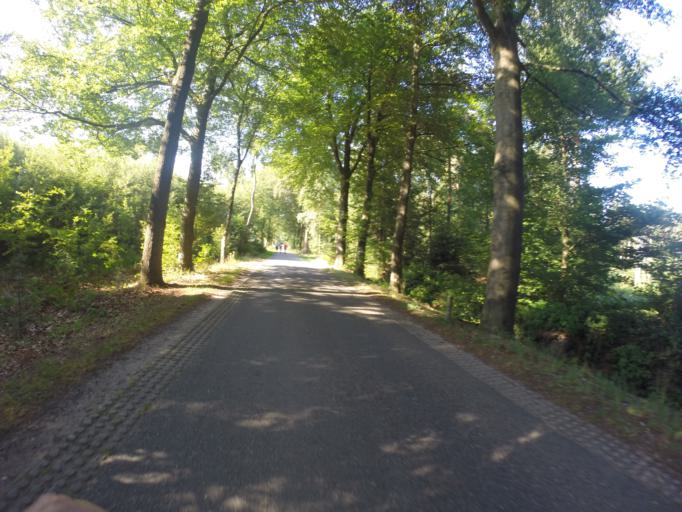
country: NL
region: Gelderland
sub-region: Gemeente Bronckhorst
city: Hengelo
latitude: 52.0954
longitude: 6.3485
